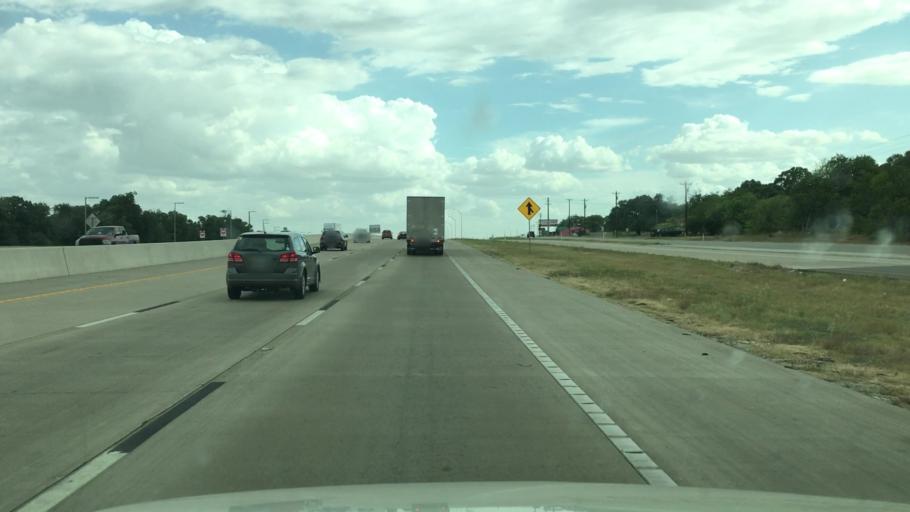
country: US
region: Texas
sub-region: McLennan County
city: Lorena
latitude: 31.3678
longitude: -97.2164
